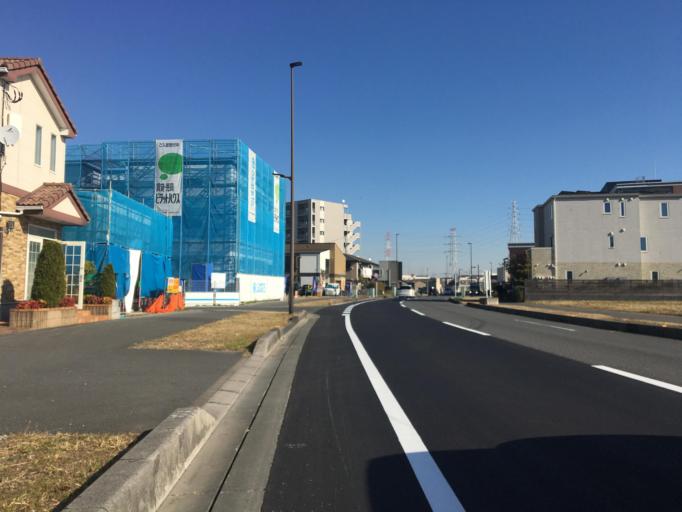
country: JP
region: Saitama
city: Yashio-shi
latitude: 35.8132
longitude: 139.8495
